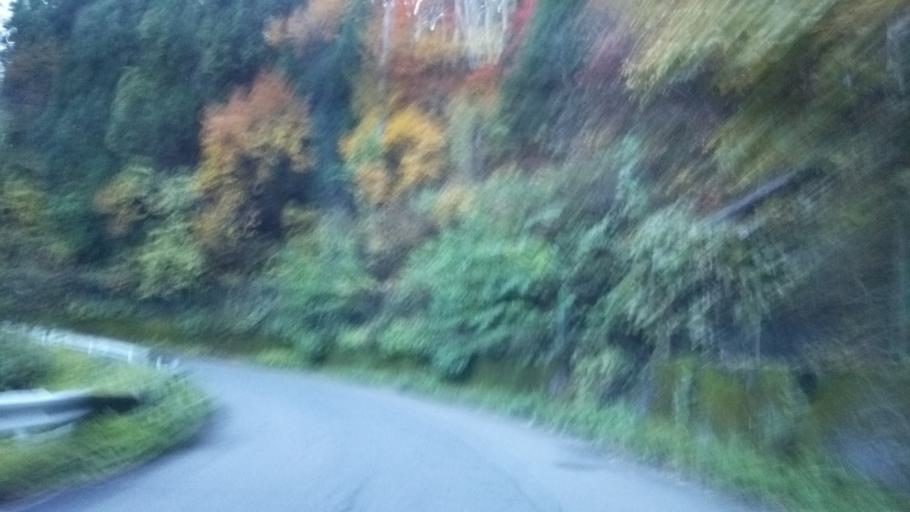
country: JP
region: Fukushima
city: Kitakata
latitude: 37.4955
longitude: 139.6603
